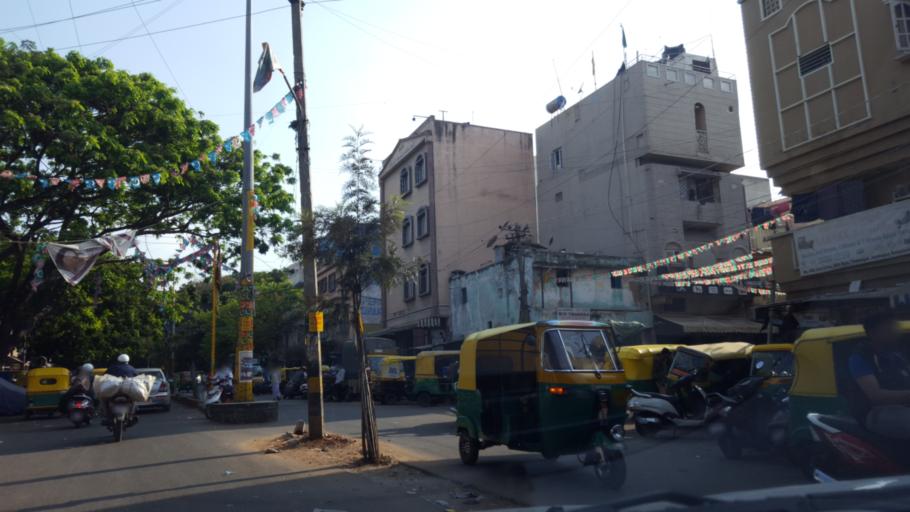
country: IN
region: Karnataka
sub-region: Bangalore Urban
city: Bangalore
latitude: 12.9280
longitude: 77.5936
